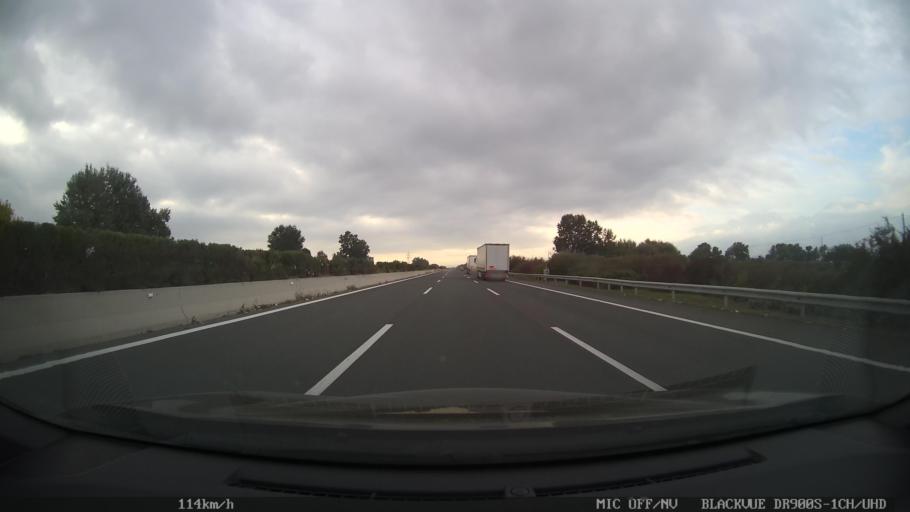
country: GR
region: Central Macedonia
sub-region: Nomos Pierias
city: Nea Efesos
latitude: 40.2220
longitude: 22.5411
